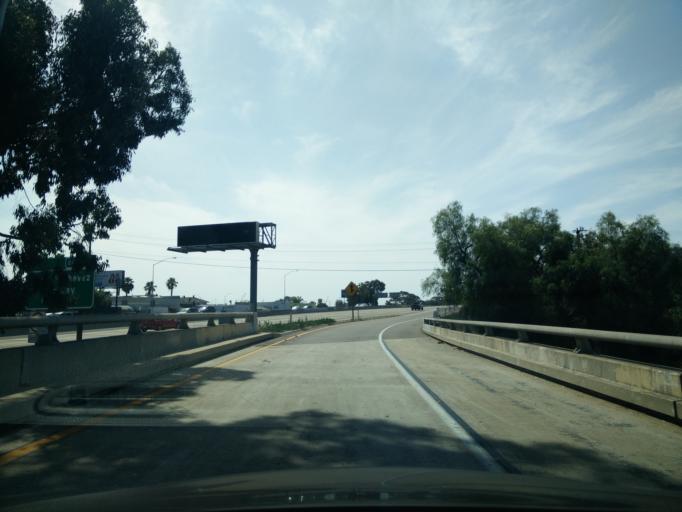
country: US
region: California
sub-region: San Diego County
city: San Diego
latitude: 32.7081
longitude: -117.1481
